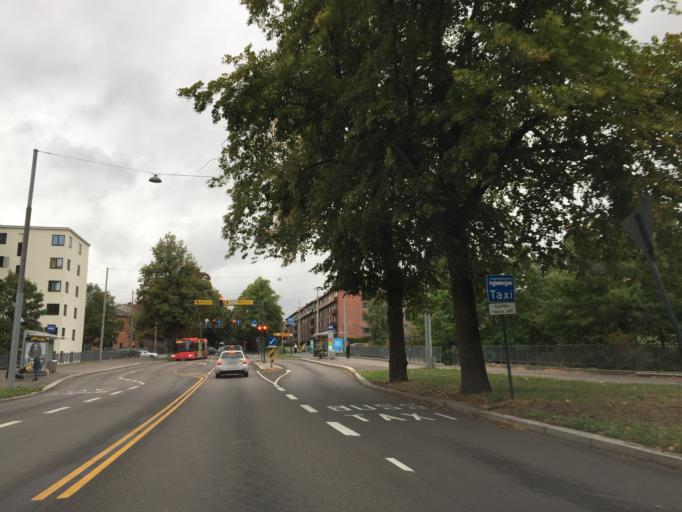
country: NO
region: Oslo
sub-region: Oslo
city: Oslo
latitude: 59.9289
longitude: 10.7703
